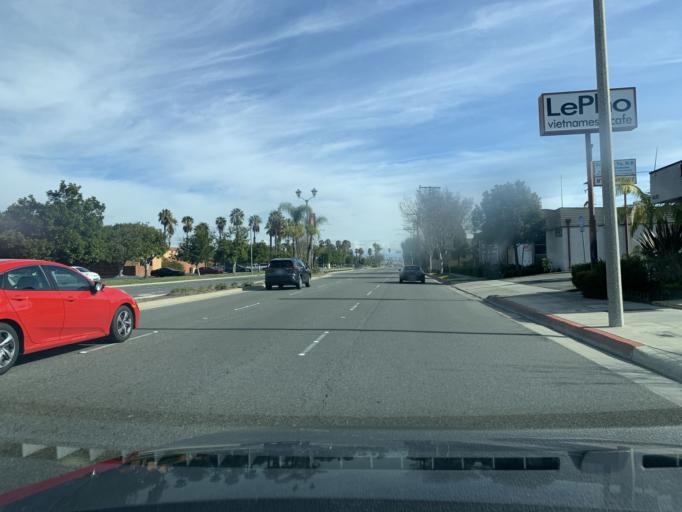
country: US
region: California
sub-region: Orange County
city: Westminster
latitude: 33.7443
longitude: -118.0153
